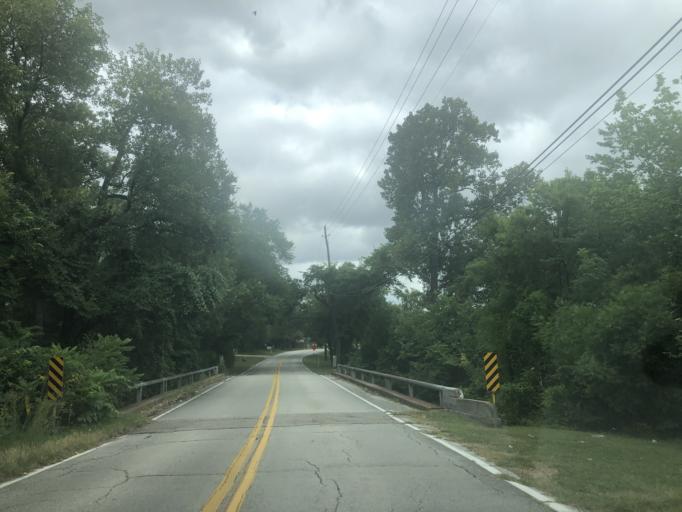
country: US
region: Texas
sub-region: Dallas County
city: Duncanville
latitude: 32.6348
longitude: -96.9184
